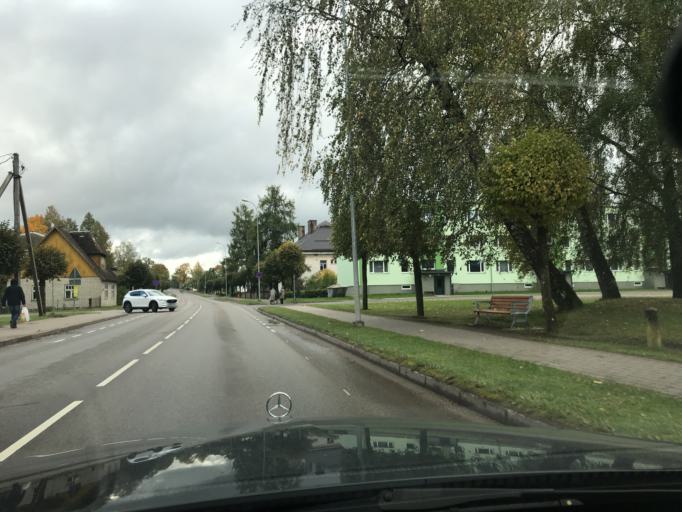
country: EE
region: Valgamaa
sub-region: Torva linn
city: Torva
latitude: 58.0020
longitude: 25.9243
